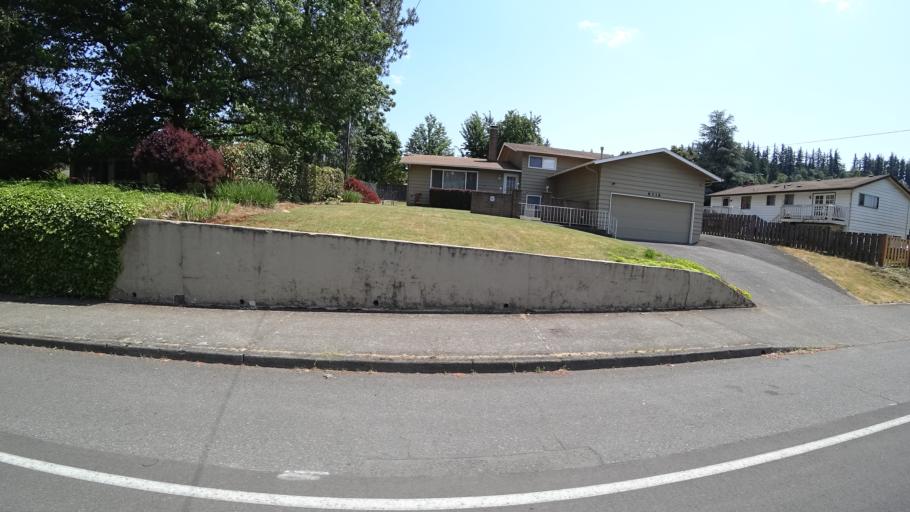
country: US
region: Oregon
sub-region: Multnomah County
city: Lents
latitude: 45.4618
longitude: -122.5686
